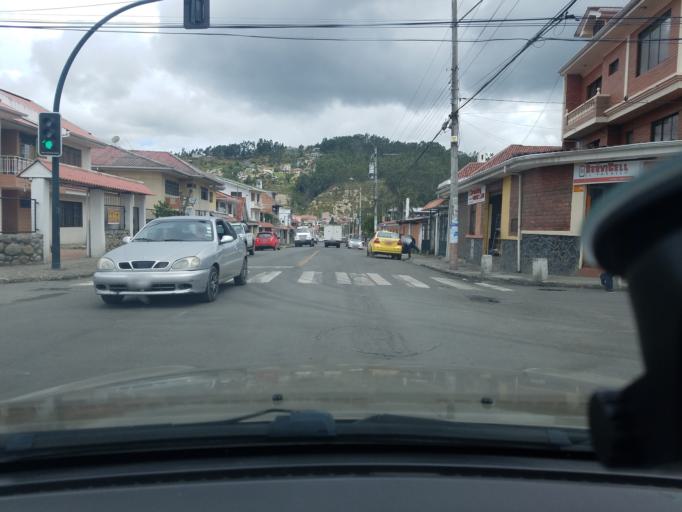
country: EC
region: Azuay
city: Cuenca
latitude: -2.9047
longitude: -78.9866
